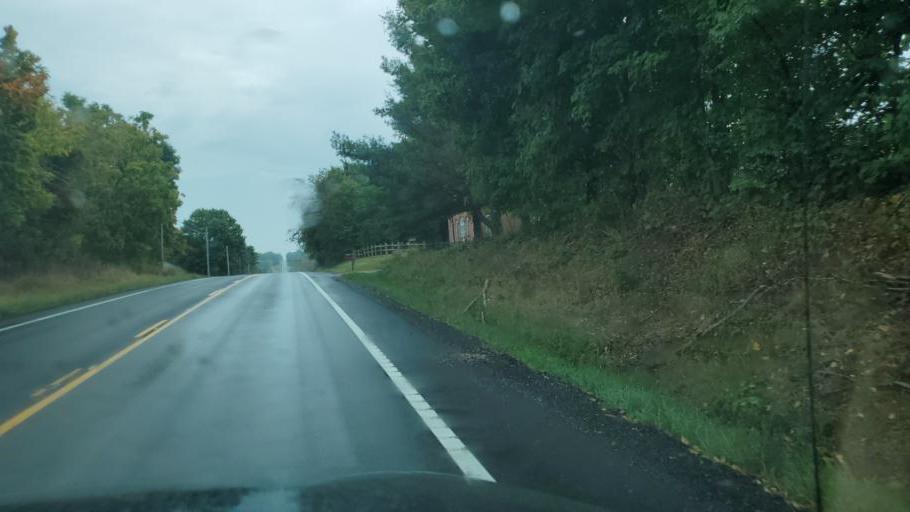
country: US
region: Ohio
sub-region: Licking County
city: Harbor Hills
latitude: 39.9590
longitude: -82.4050
